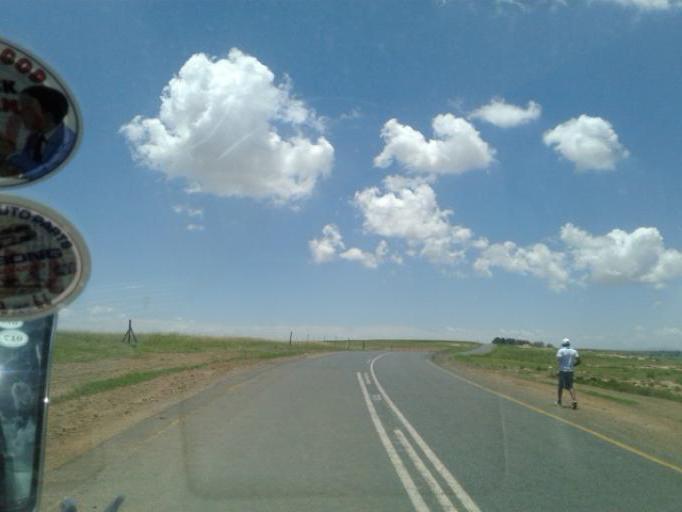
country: LS
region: Maseru
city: Maseru
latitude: -29.3011
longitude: 27.6119
